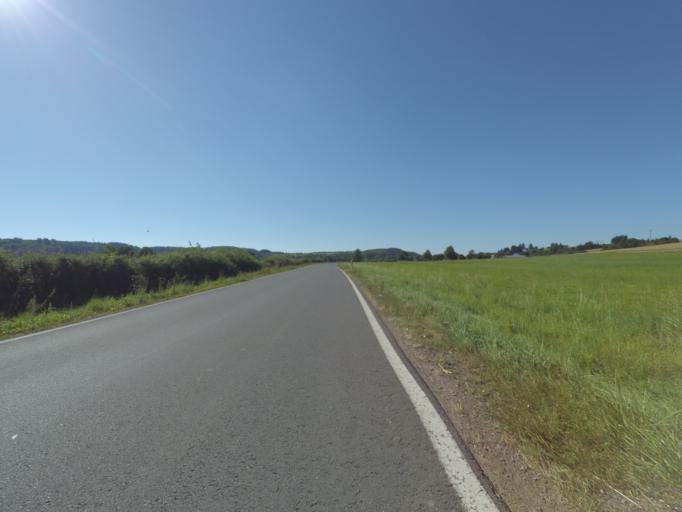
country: DE
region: Rheinland-Pfalz
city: Strohn
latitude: 50.1185
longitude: 6.9133
